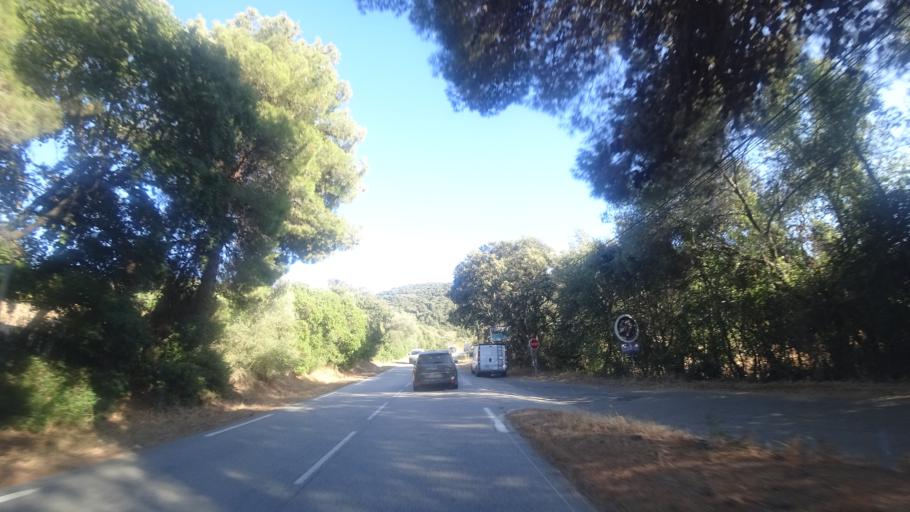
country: FR
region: Corsica
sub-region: Departement de la Corse-du-Sud
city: Cargese
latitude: 42.1716
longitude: 8.6085
